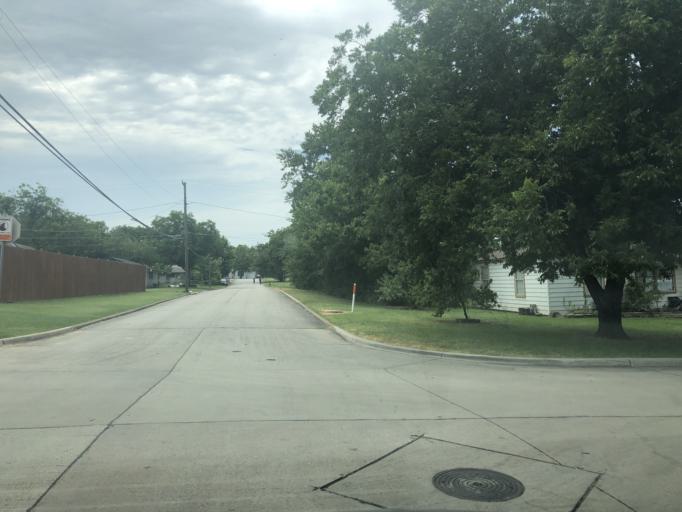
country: US
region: Texas
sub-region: Dallas County
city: Grand Prairie
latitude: 32.7353
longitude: -97.0037
